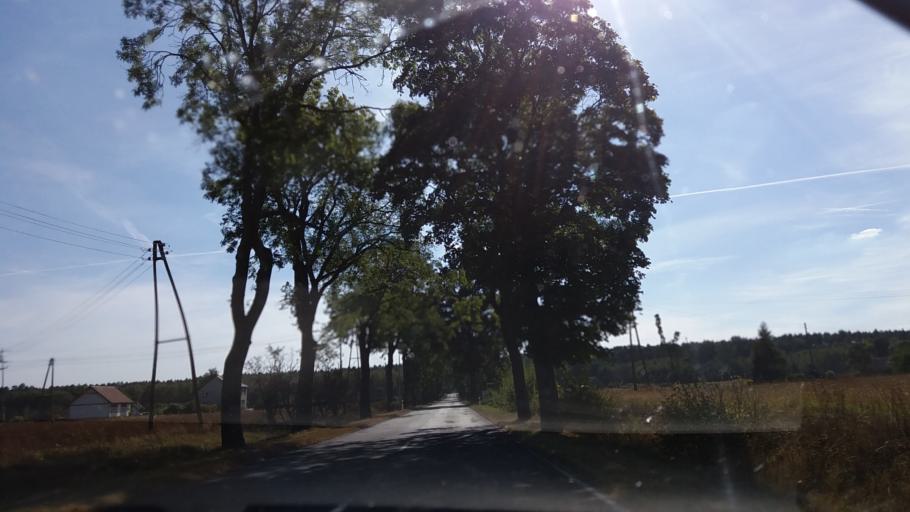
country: PL
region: Lubusz
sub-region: Powiat strzelecko-drezdenecki
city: Drezdenko
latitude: 52.7457
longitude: 15.8580
